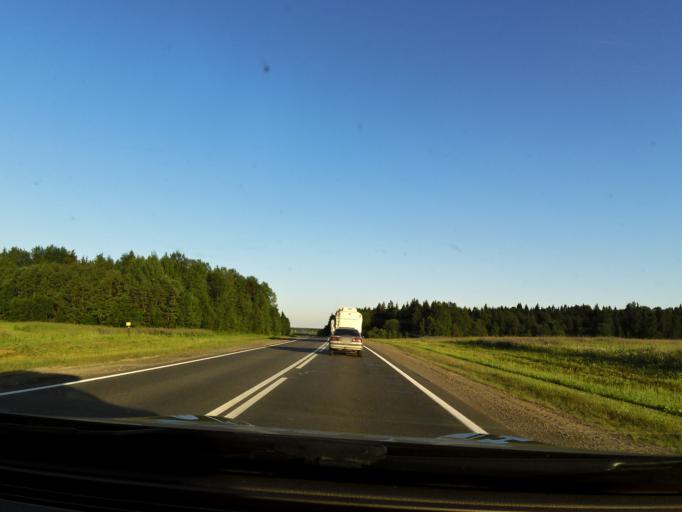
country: RU
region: Vologda
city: Gryazovets
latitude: 58.8362
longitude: 40.2081
